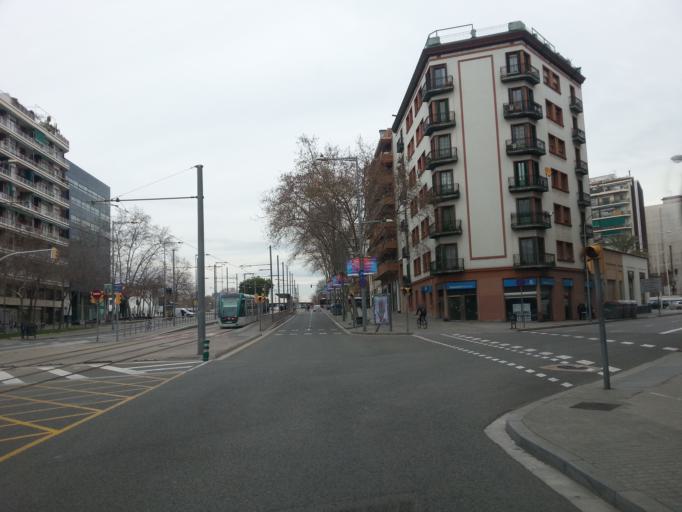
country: ES
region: Catalonia
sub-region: Provincia de Barcelona
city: Ciutat Vella
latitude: 41.3932
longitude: 2.1870
